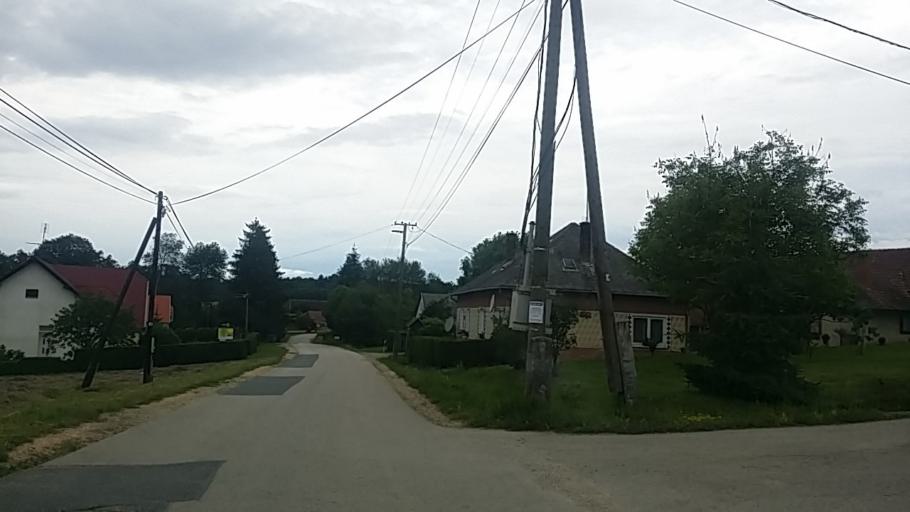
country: SI
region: Hodos-Hodos
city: Hodos
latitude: 46.8466
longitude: 16.4164
